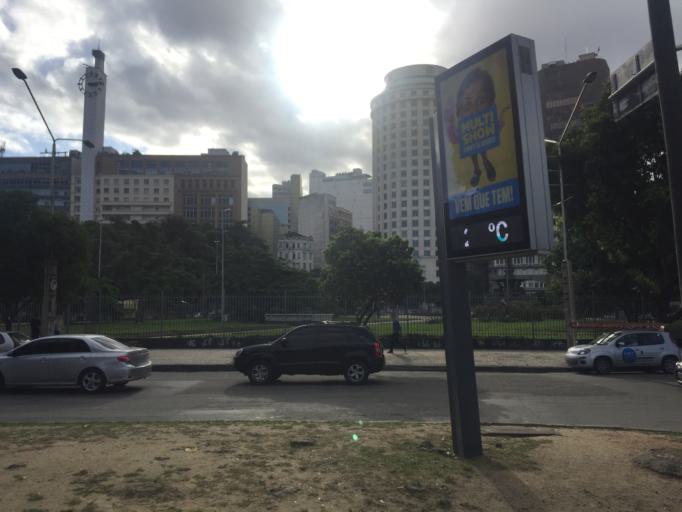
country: BR
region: Rio de Janeiro
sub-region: Rio De Janeiro
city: Rio de Janeiro
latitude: -22.9132
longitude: -43.1749
